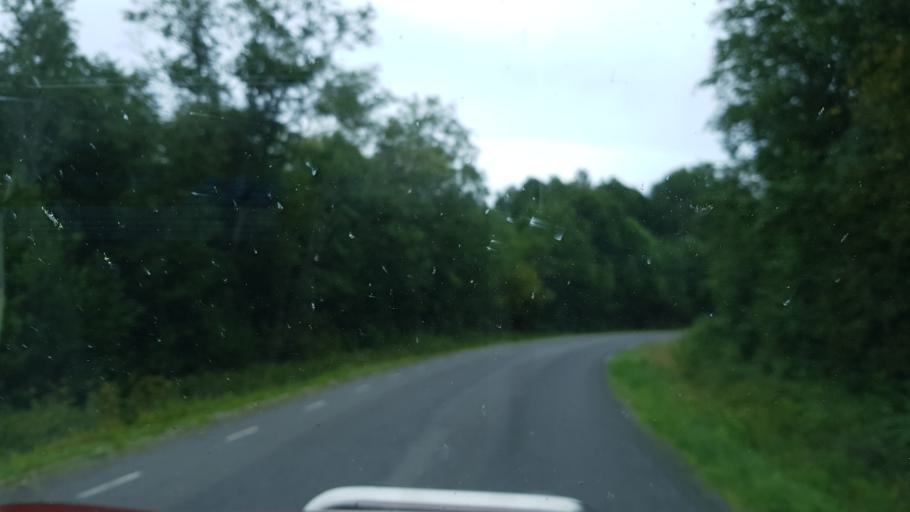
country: EE
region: Laeaene
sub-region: Lihula vald
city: Lihula
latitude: 58.8764
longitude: 23.8753
